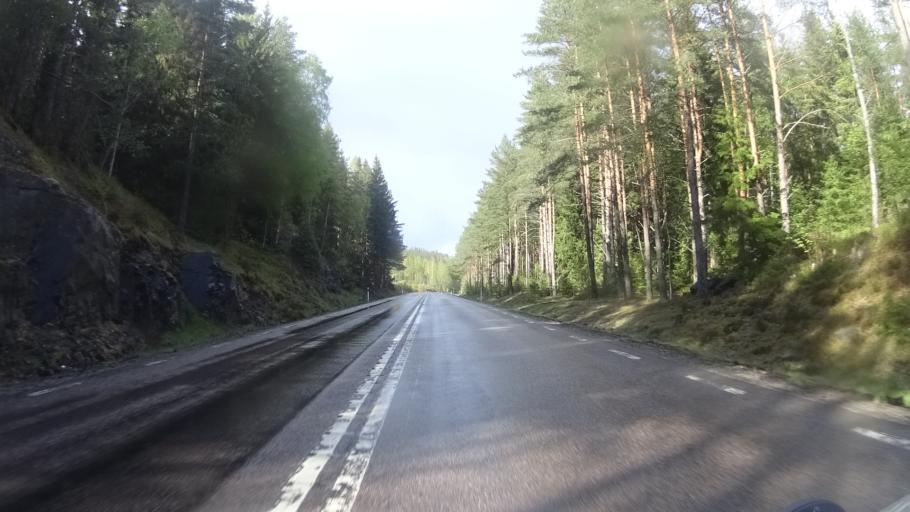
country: SE
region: OErebro
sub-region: Askersunds Kommun
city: Askersund
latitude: 58.7391
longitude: 14.7786
